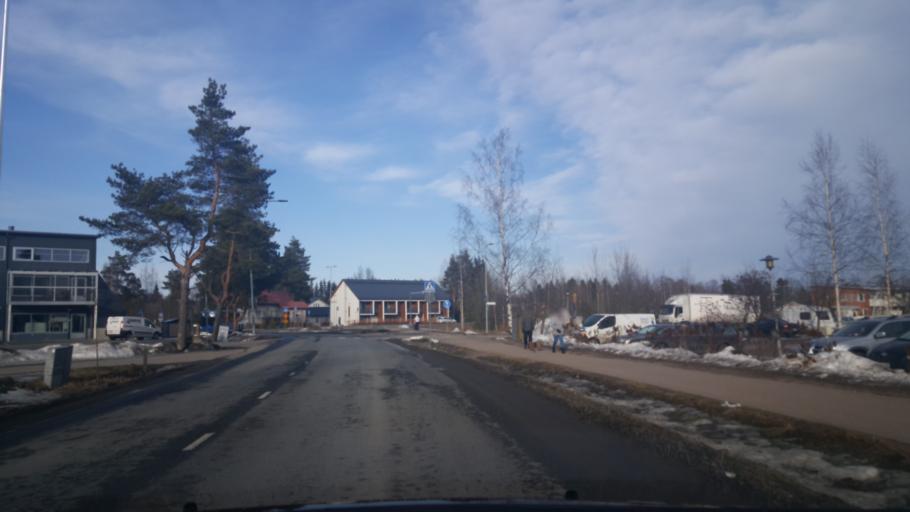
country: FI
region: Uusimaa
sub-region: Helsinki
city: Vantaa
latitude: 60.2911
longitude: 25.0089
